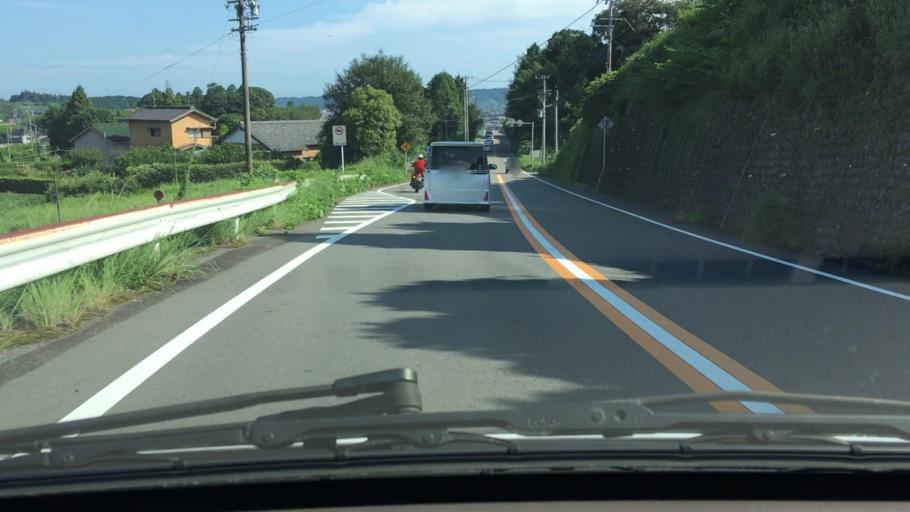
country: JP
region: Shizuoka
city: Kanaya
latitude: 34.8608
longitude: 138.1122
